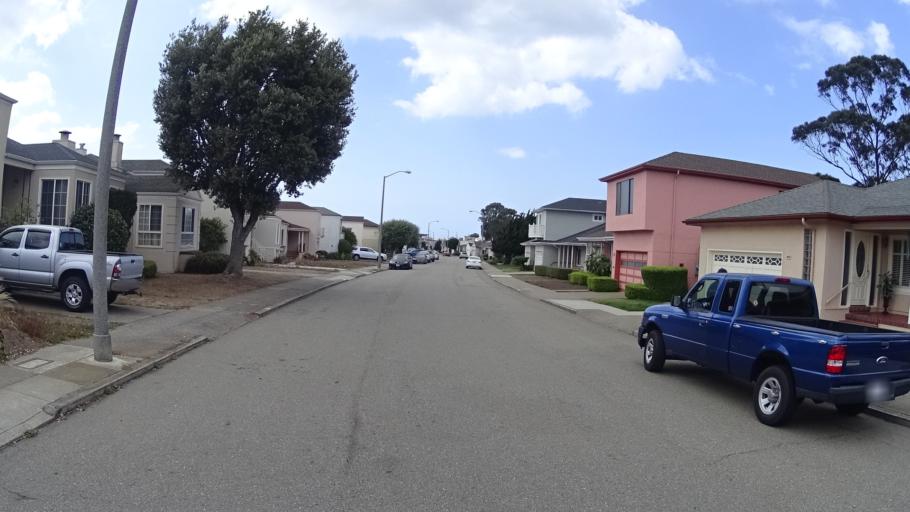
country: US
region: California
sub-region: San Mateo County
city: Daly City
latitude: 37.7350
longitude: -122.4863
